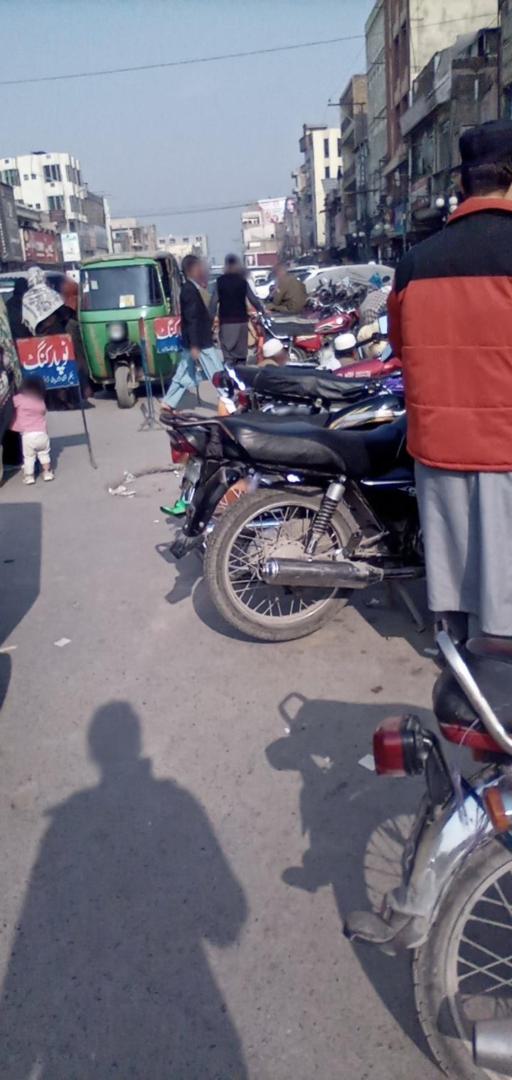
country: PK
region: Khyber Pakhtunkhwa
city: Peshawar
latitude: 33.9976
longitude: 71.5384
